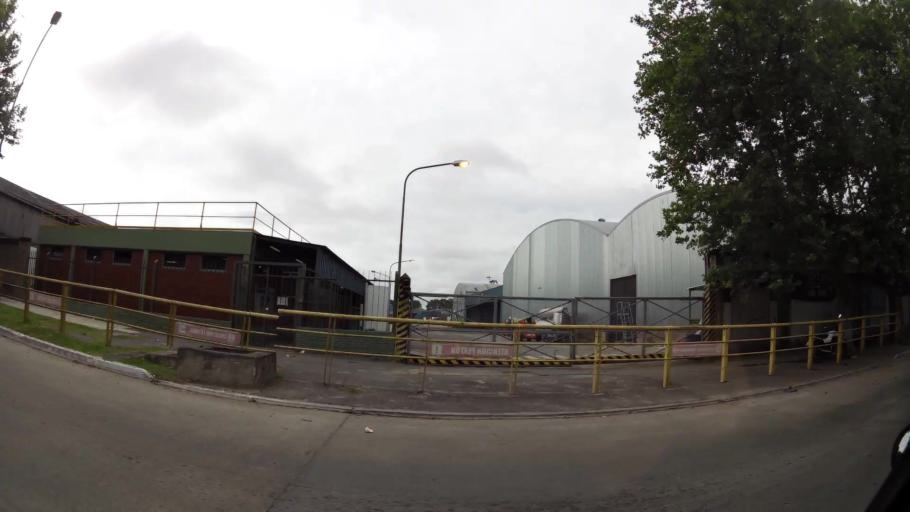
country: AR
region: Buenos Aires
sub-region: Partido de Quilmes
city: Quilmes
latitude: -34.7314
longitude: -58.2571
